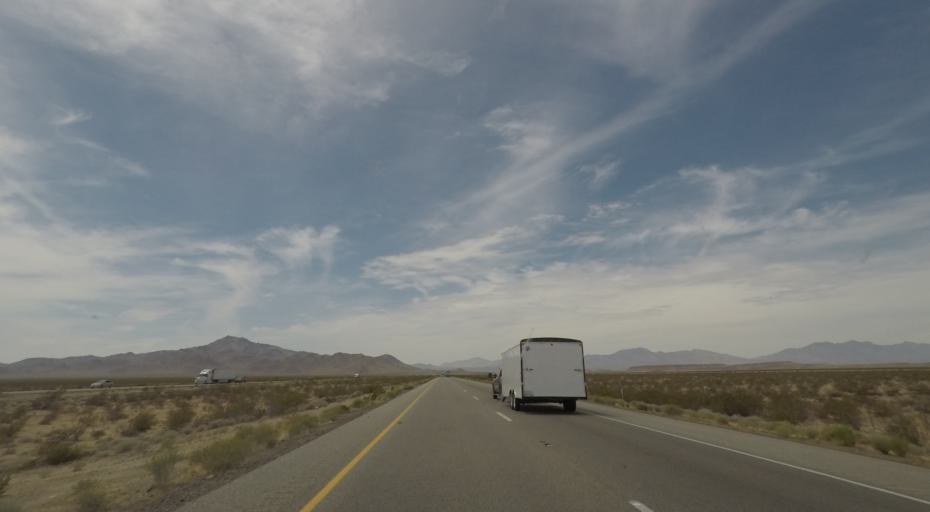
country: US
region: California
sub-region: San Bernardino County
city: Needles
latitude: 34.8054
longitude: -115.2694
